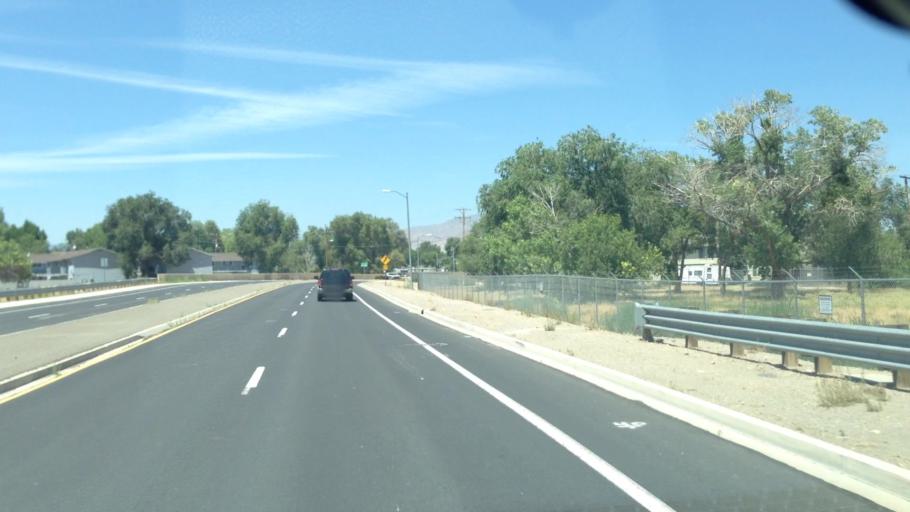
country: US
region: Nevada
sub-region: Washoe County
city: Sparks
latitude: 39.4913
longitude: -119.7773
